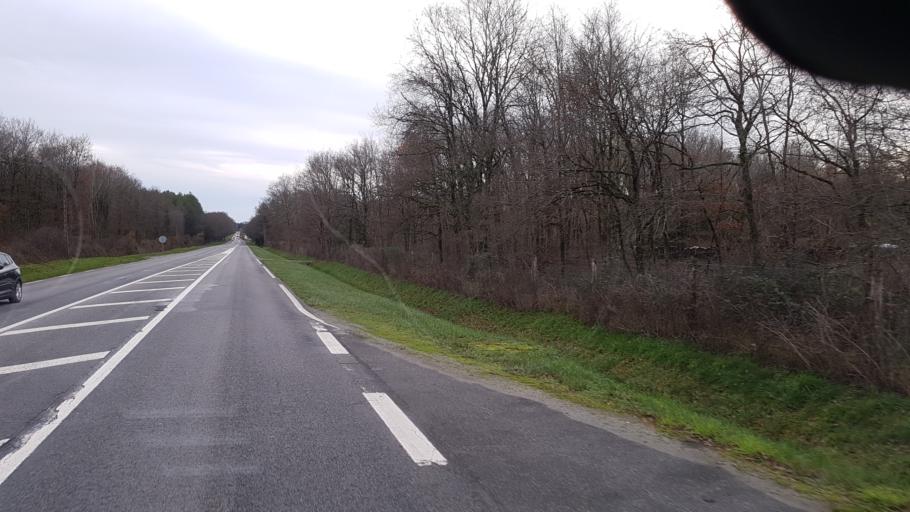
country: FR
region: Centre
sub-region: Departement du Loir-et-Cher
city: Nouan-le-Fuzelier
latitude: 47.5530
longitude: 2.0339
